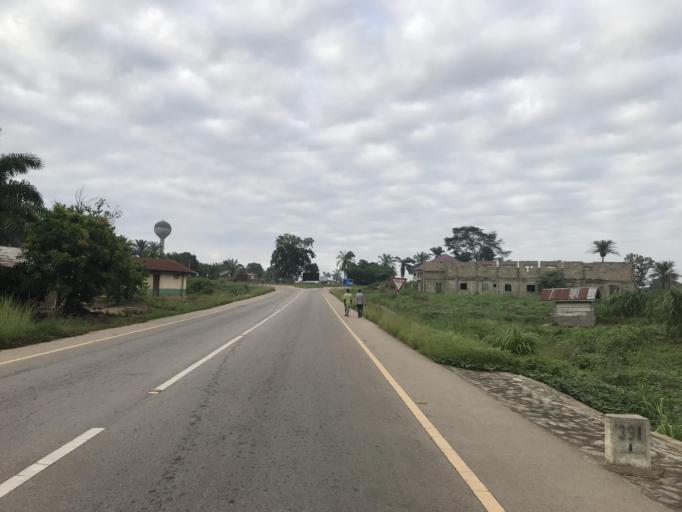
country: SL
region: Eastern Province
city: Pendembu
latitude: 8.0929
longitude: -10.6941
